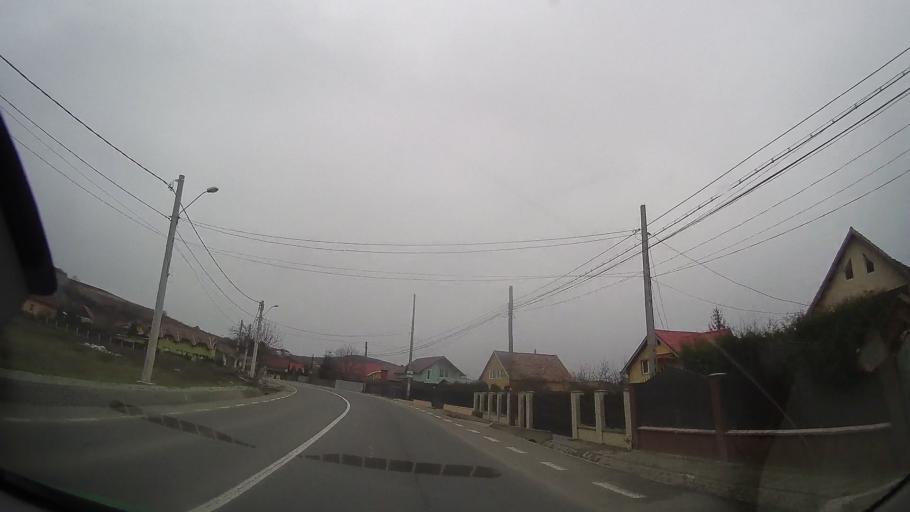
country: RO
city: Remetea
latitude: 46.6015
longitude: 24.5304
